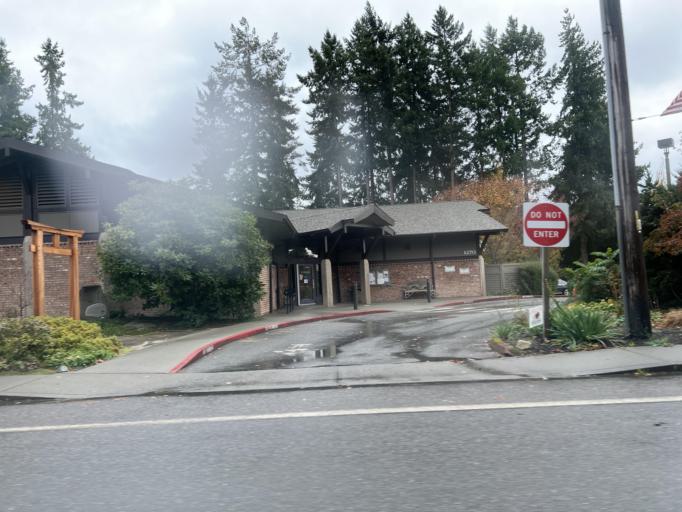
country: US
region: Washington
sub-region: Kitsap County
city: Bainbridge Island
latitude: 47.6352
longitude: -122.5210
